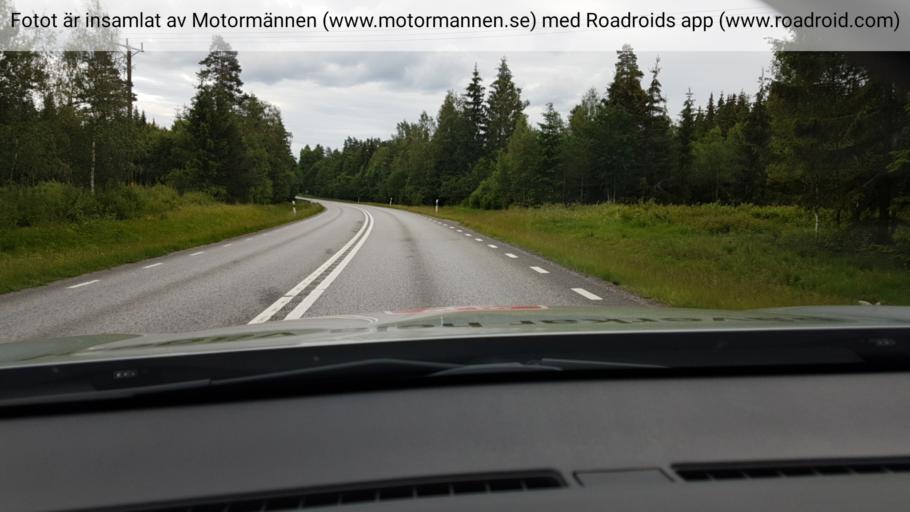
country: SE
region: Joenkoeping
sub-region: Mullsjo Kommun
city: Mullsjoe
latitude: 58.0186
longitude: 13.8275
